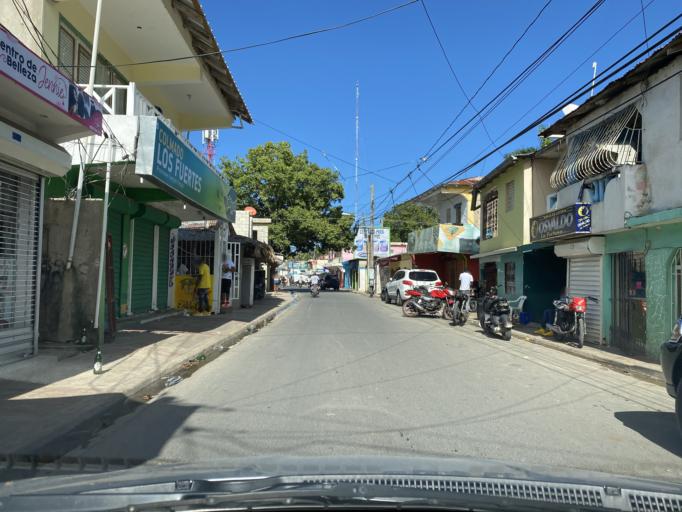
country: DO
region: Samana
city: Las Terrenas
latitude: 19.3125
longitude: -69.5419
